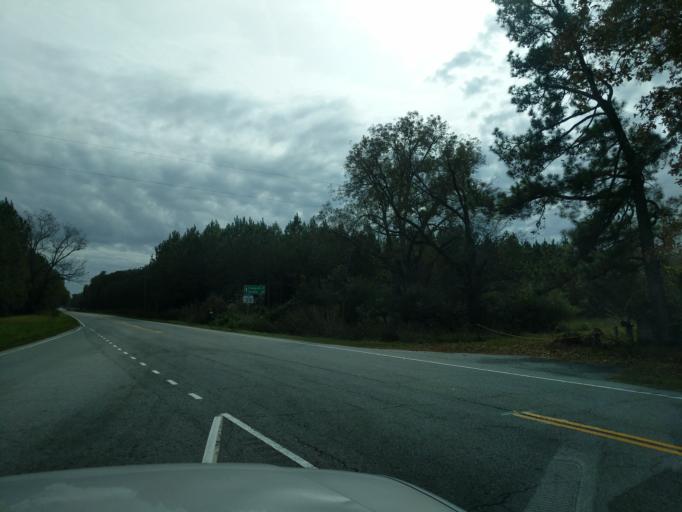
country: US
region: South Carolina
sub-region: Greenwood County
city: Ninety Six
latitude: 34.1993
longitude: -81.8860
